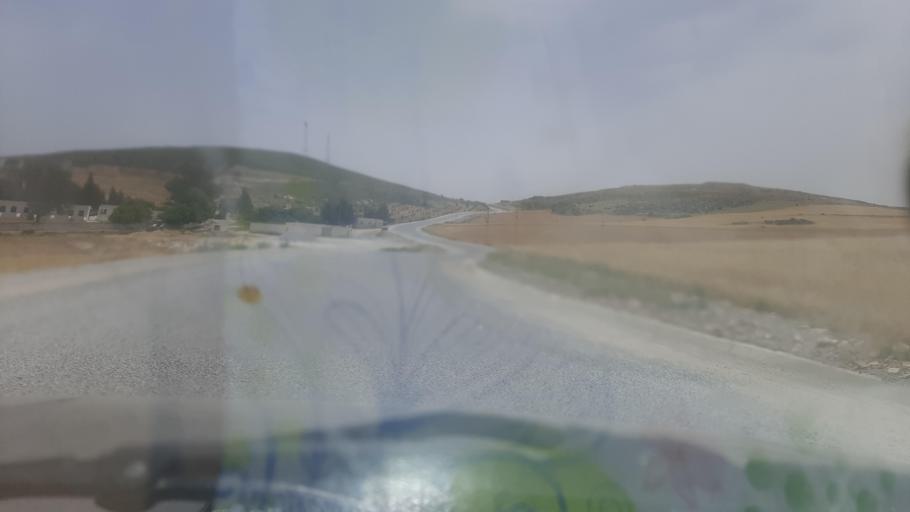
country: TN
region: Zaghwan
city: Zaghouan
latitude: 36.5383
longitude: 10.1530
